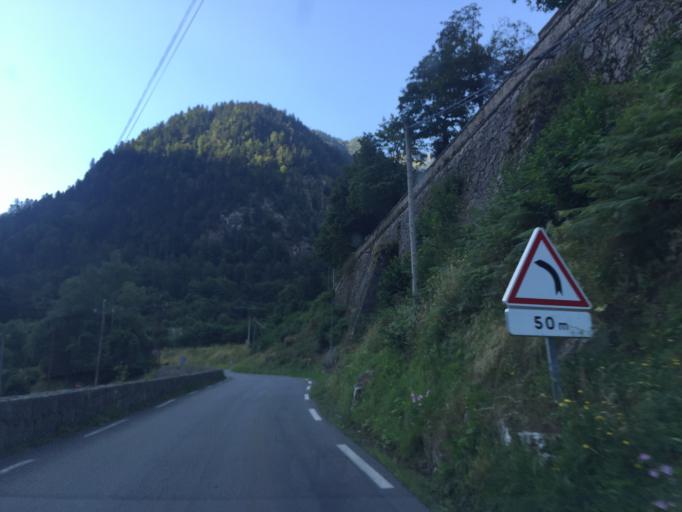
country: FR
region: Midi-Pyrenees
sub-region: Departement des Hautes-Pyrenees
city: Cauterets
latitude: 42.8755
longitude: -0.1096
